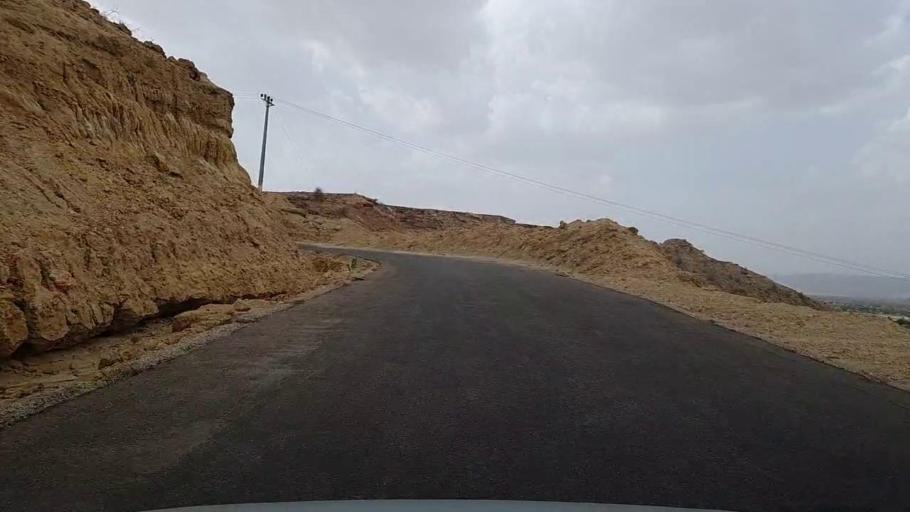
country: PK
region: Sindh
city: Jamshoro
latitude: 25.4272
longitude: 67.6921
